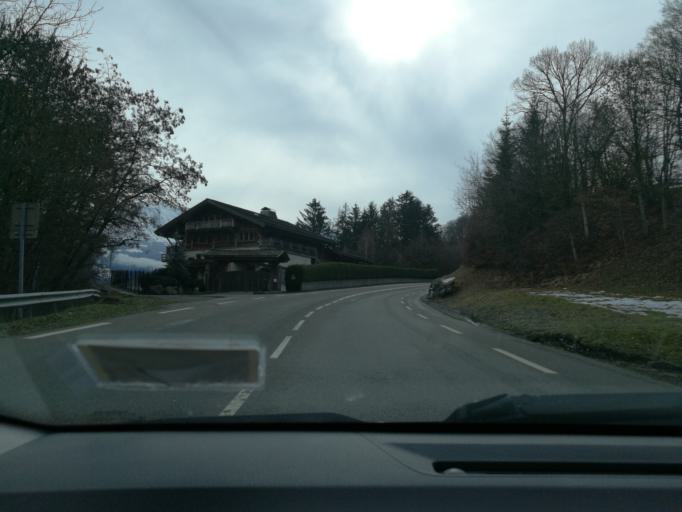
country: FR
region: Rhone-Alpes
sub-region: Departement de la Haute-Savoie
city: Domancy
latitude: 45.9253
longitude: 6.6328
